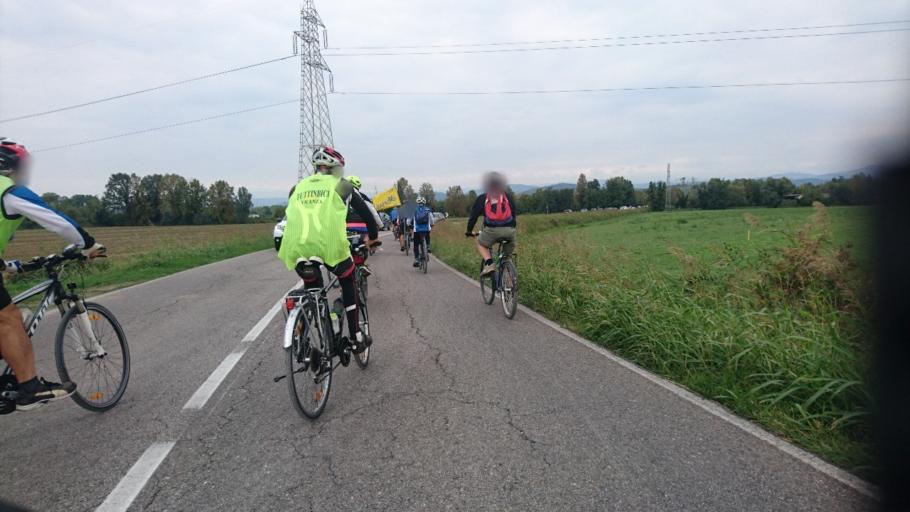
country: IT
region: Veneto
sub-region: Provincia di Verona
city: Zevio
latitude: 45.3991
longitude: 11.1253
